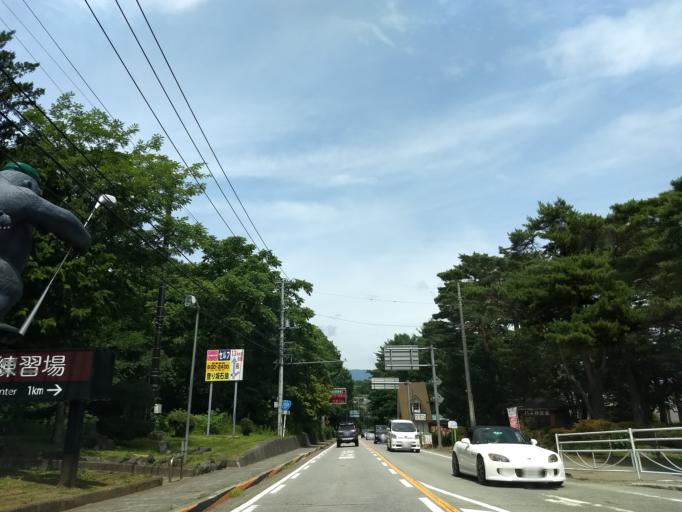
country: JP
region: Yamanashi
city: Fujikawaguchiko
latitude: 35.4568
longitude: 138.8056
